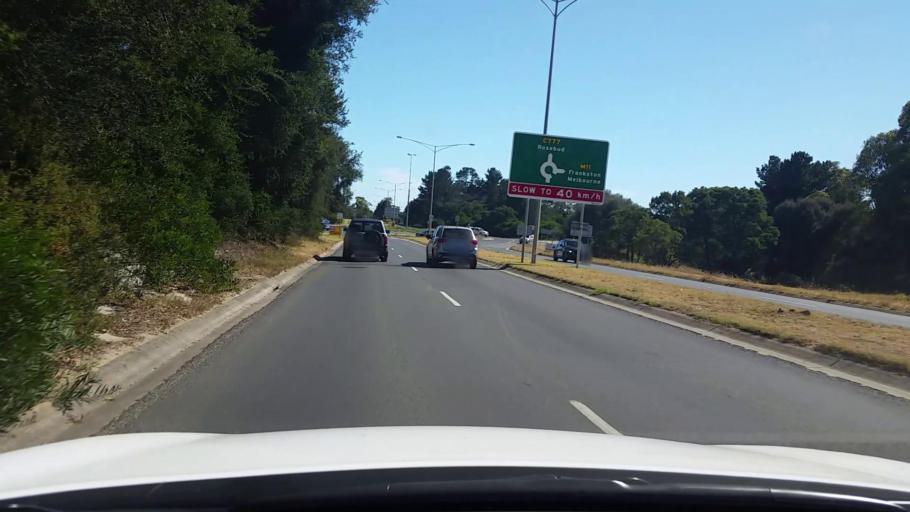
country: AU
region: Victoria
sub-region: Mornington Peninsula
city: Rosebud West
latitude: -38.3781
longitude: 144.8890
